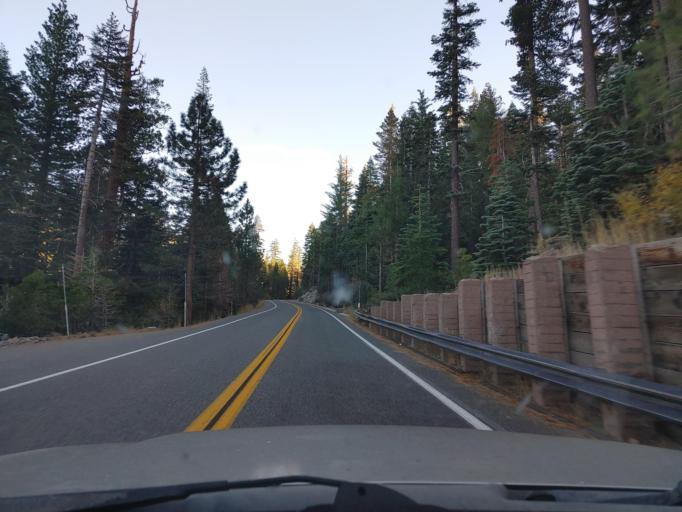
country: US
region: California
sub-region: Placer County
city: Tahoma
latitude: 38.9831
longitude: -120.1072
